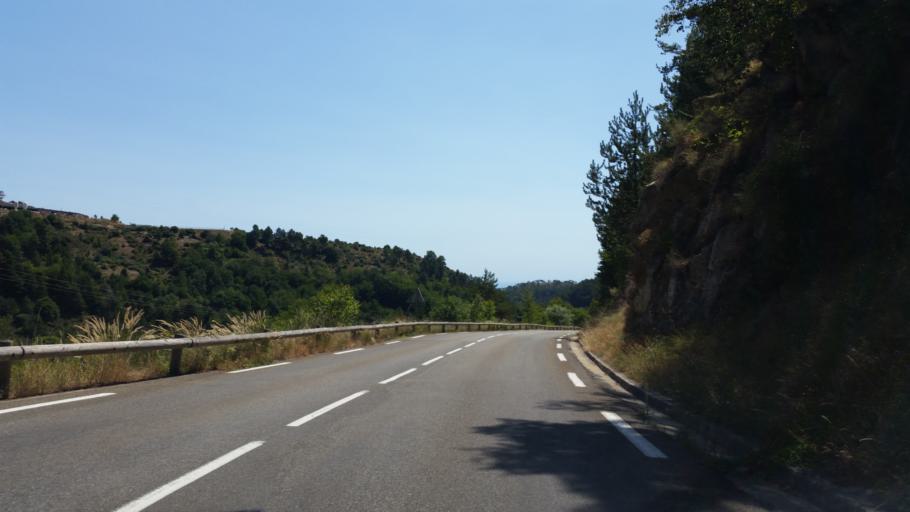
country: FR
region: Provence-Alpes-Cote d'Azur
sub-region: Departement des Alpes-Maritimes
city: Breil-sur-Roya
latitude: 43.9208
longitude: 7.4730
